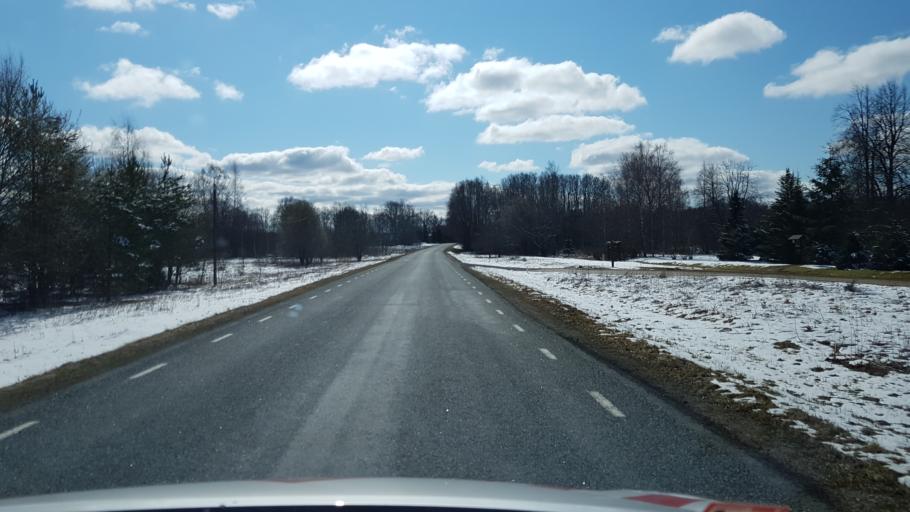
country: EE
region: Laeaene-Virumaa
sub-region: Kadrina vald
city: Kadrina
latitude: 59.4738
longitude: 25.9971
